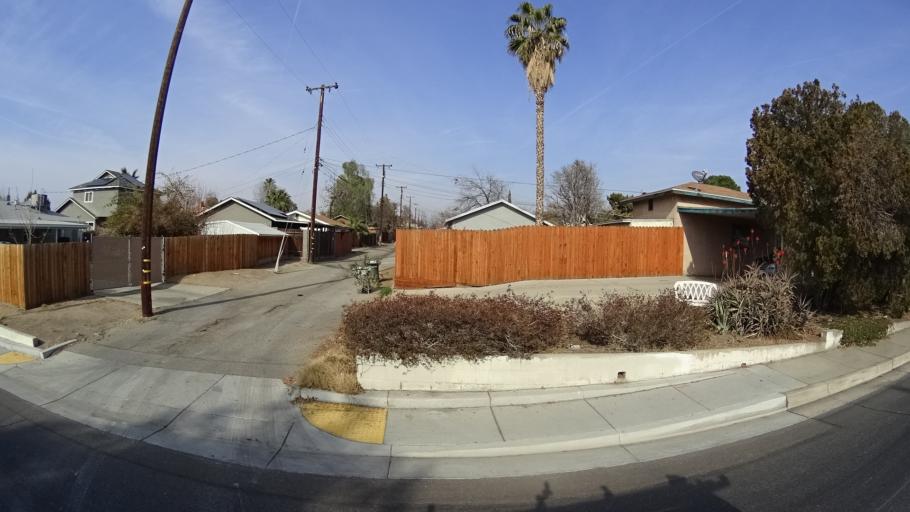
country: US
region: California
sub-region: Kern County
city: Oildale
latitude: 35.3976
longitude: -118.9778
